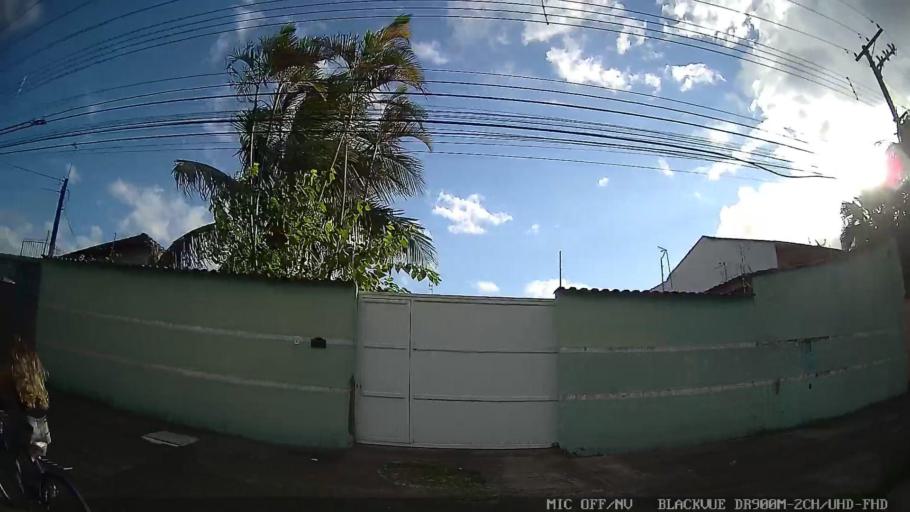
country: BR
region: Sao Paulo
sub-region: Caraguatatuba
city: Caraguatatuba
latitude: -23.6318
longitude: -45.4299
